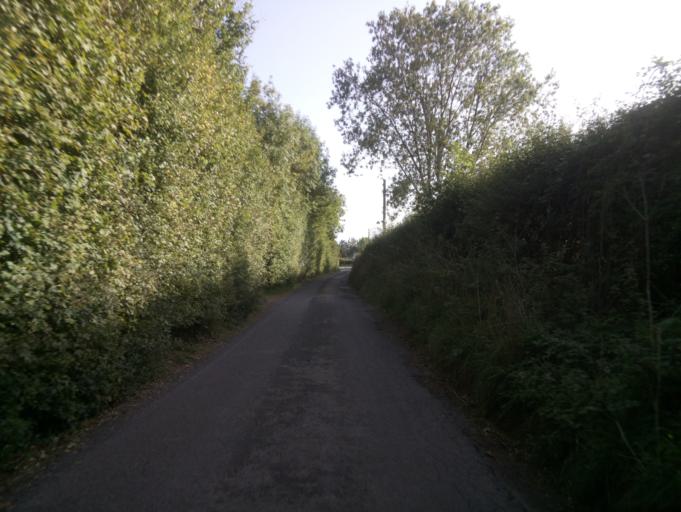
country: GB
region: England
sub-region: Gloucestershire
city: Newent
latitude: 51.9641
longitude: -2.3105
